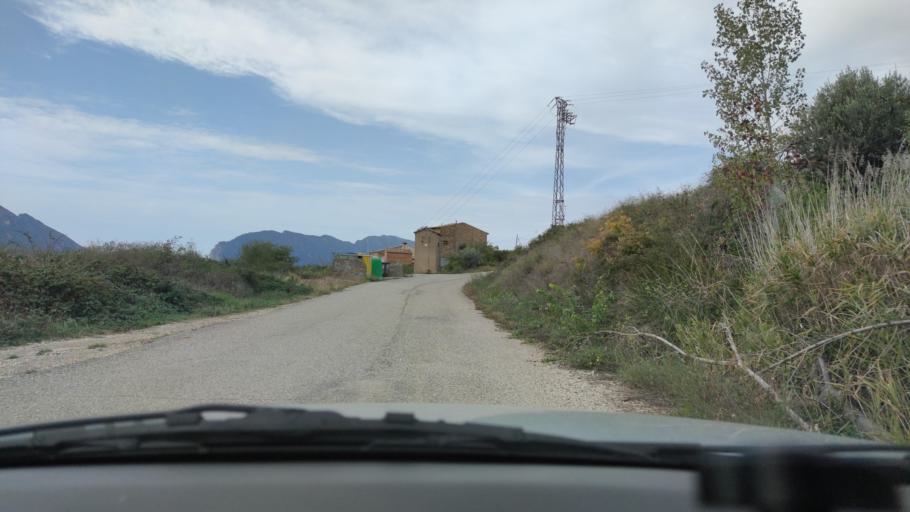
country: ES
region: Catalonia
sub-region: Provincia de Lleida
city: Llimiana
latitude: 42.0689
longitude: 0.9449
